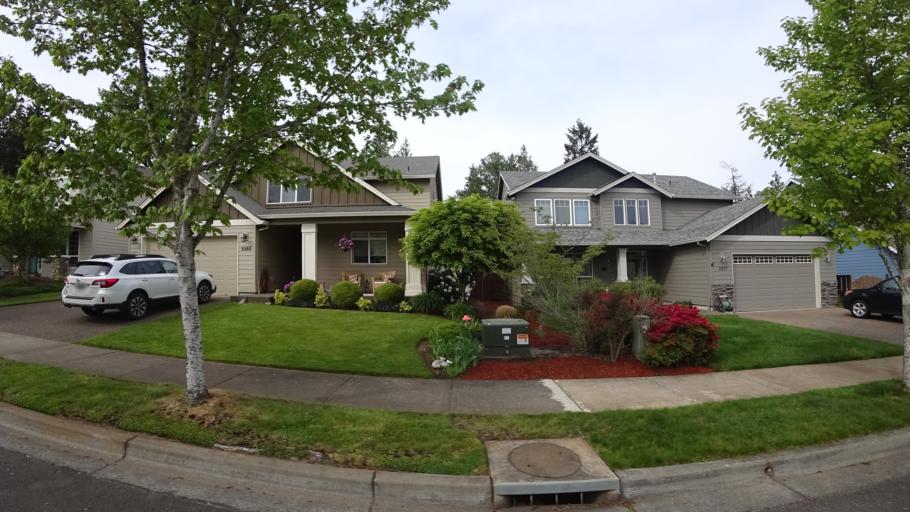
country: US
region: Oregon
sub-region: Washington County
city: Aloha
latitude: 45.5088
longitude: -122.9269
